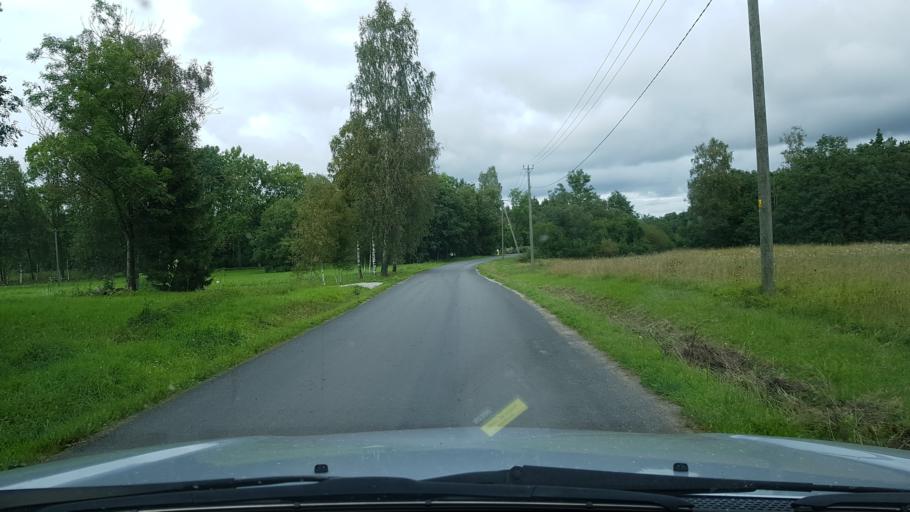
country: EE
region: Harju
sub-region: Rae vald
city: Vaida
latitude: 59.3468
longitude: 24.9601
